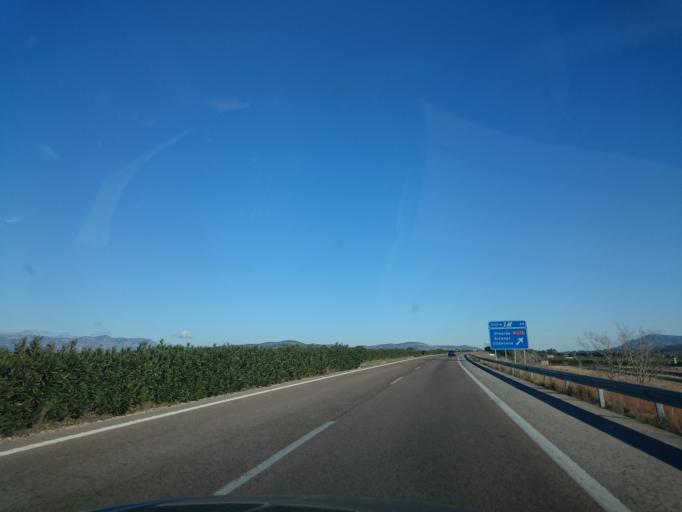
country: ES
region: Catalonia
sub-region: Provincia de Tarragona
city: Ulldecona
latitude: 40.5496
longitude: 0.4215
